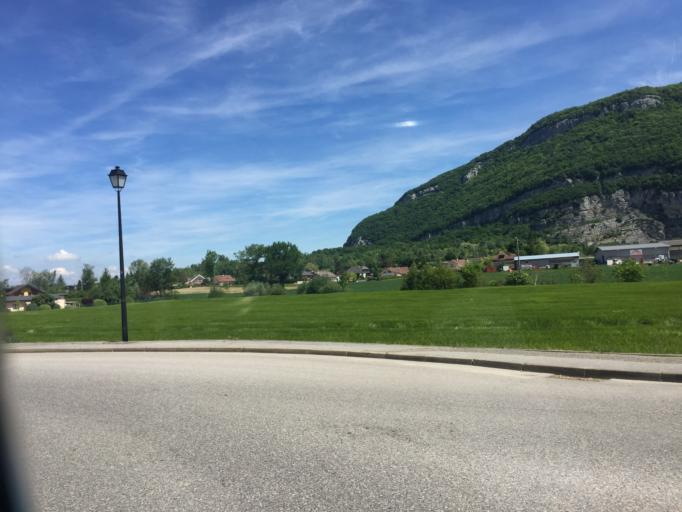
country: FR
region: Rhone-Alpes
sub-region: Departement de la Haute-Savoie
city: Sillingy
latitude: 45.9475
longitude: 6.0392
